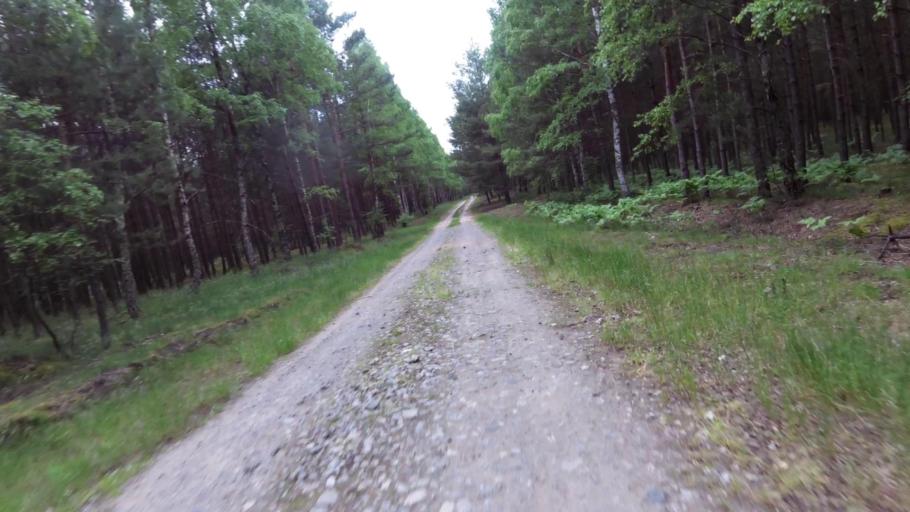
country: PL
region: West Pomeranian Voivodeship
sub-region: Powiat mysliborski
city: Debno
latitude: 52.8165
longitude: 14.6567
